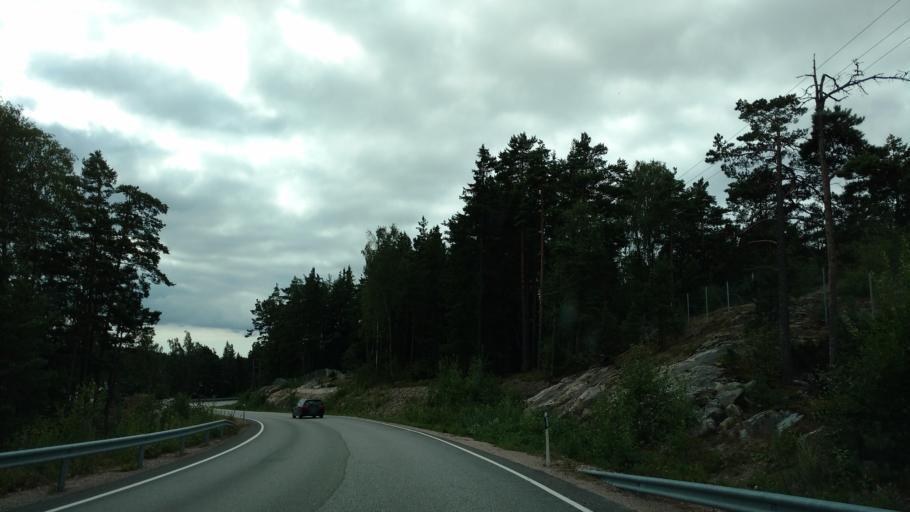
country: FI
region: Varsinais-Suomi
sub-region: Aboland-Turunmaa
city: Dragsfjaerd
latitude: 59.9825
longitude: 22.4511
